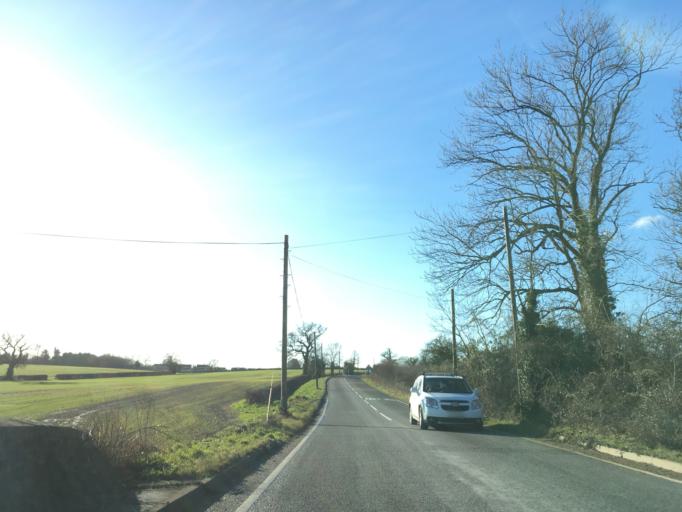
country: GB
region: England
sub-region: Wiltshire
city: Charlton
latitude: 51.5936
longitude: -2.0778
